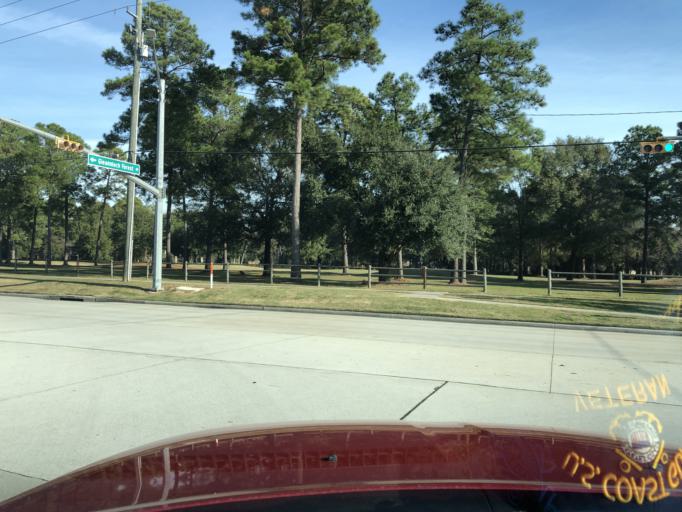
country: US
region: Texas
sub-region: Harris County
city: Tomball
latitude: 30.0369
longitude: -95.5613
